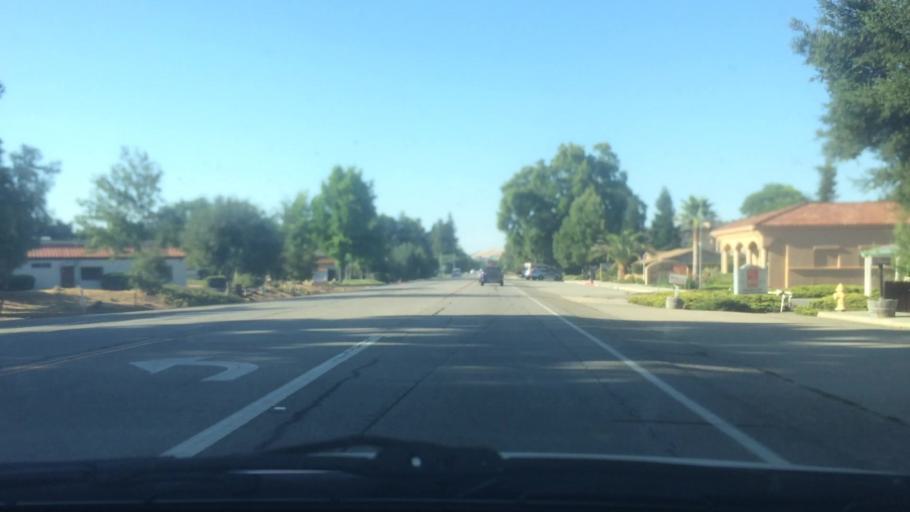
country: US
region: California
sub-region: San Luis Obispo County
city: Atascadero
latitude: 35.4713
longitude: -120.6691
